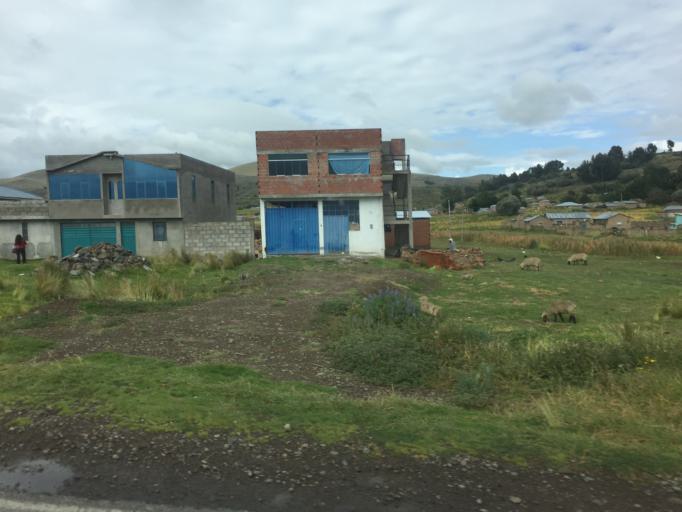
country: PE
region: Puno
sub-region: Provincia de Chucuito
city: Juli
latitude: -16.2141
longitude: -69.3960
